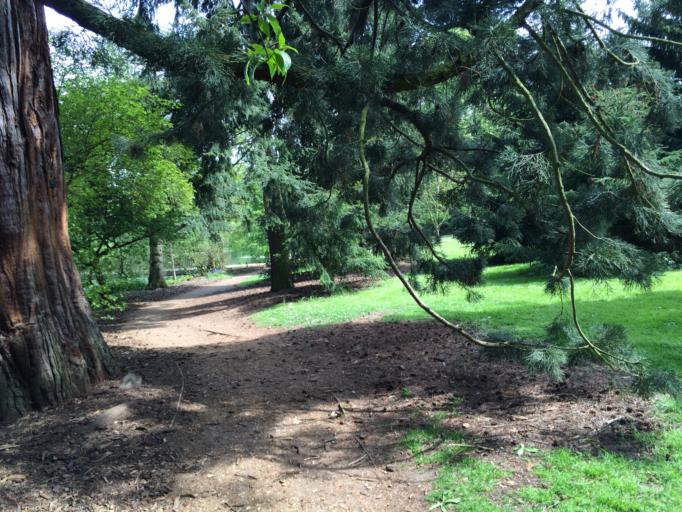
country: GB
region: England
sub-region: Greater London
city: Brentford
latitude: 51.4765
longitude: -0.2999
